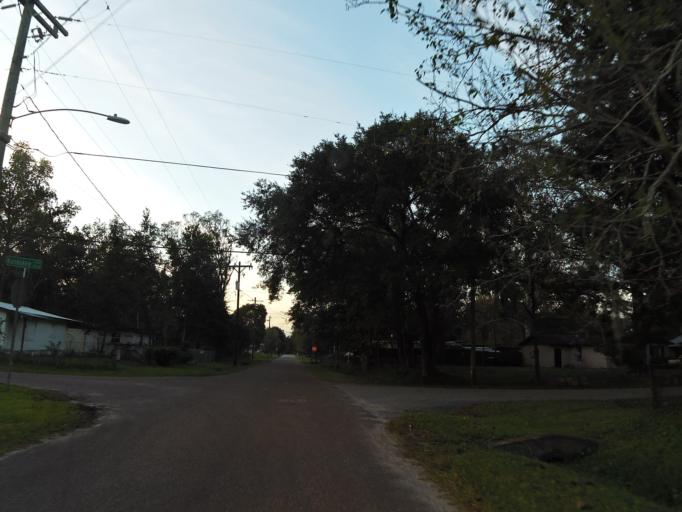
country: US
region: Florida
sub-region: Duval County
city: Jacksonville
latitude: 30.3564
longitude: -81.7351
